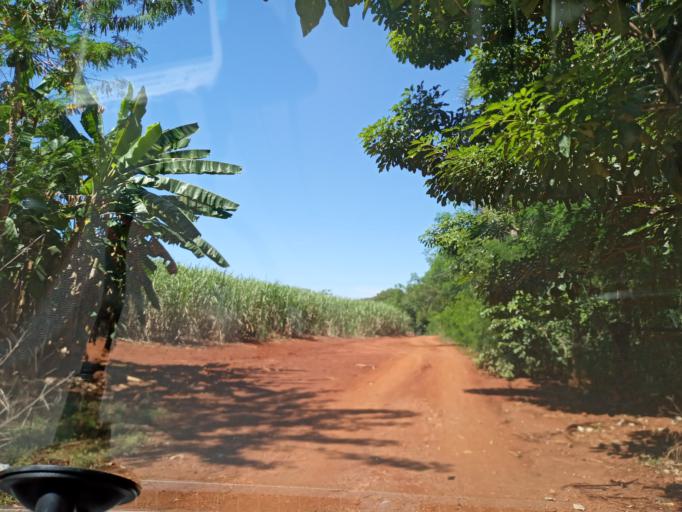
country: BR
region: Goias
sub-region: Itumbiara
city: Itumbiara
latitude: -18.4385
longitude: -49.1421
